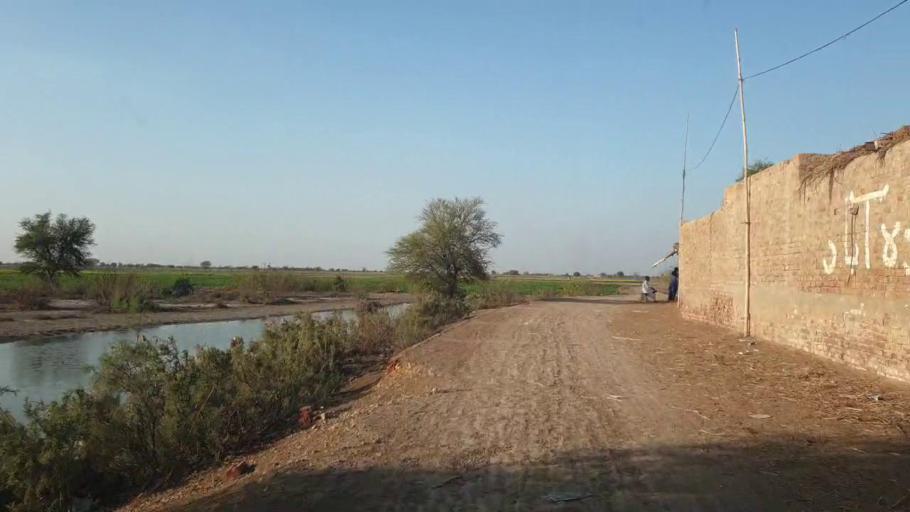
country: PK
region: Sindh
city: Tando Allahyar
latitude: 25.3778
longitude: 68.7083
